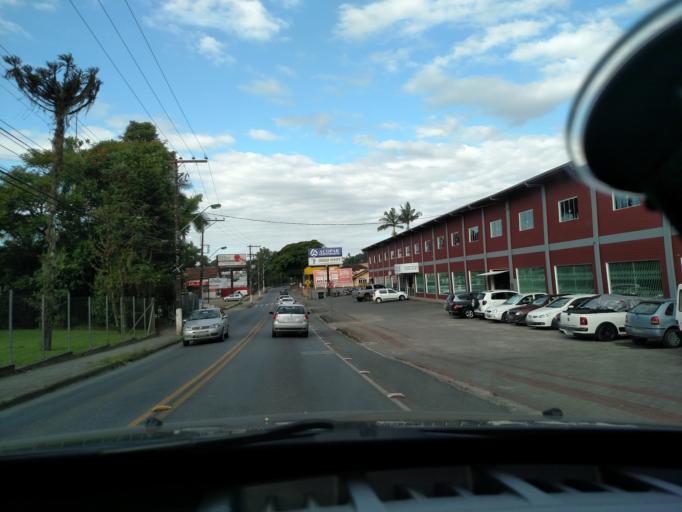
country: BR
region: Santa Catarina
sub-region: Blumenau
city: Blumenau
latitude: -26.8892
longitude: -49.0866
